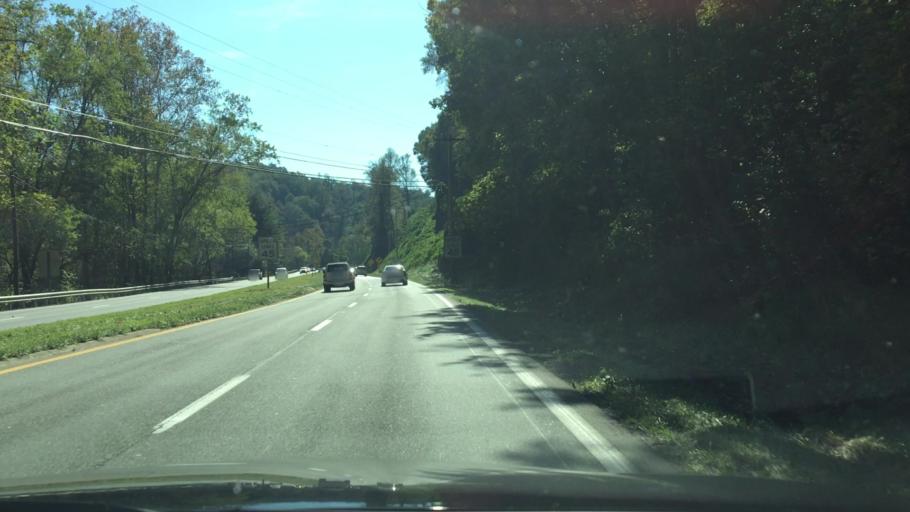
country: US
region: Virginia
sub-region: Roanoke County
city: Narrows
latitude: 37.1246
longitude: -79.9589
